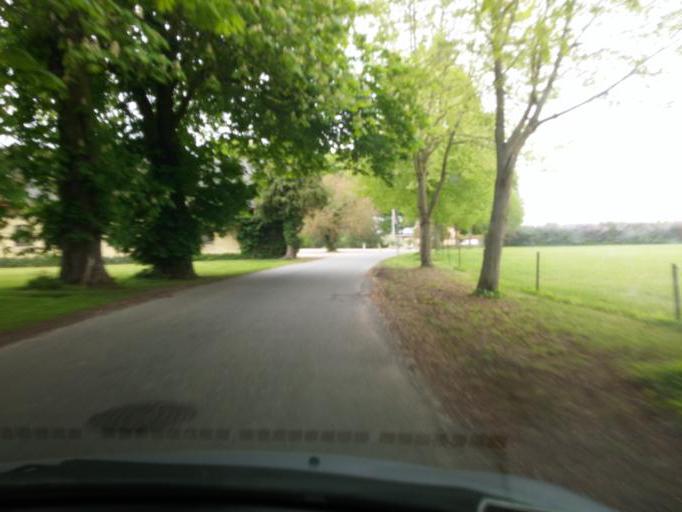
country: DK
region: South Denmark
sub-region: Odense Kommune
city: Bullerup
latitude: 55.4096
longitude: 10.5060
